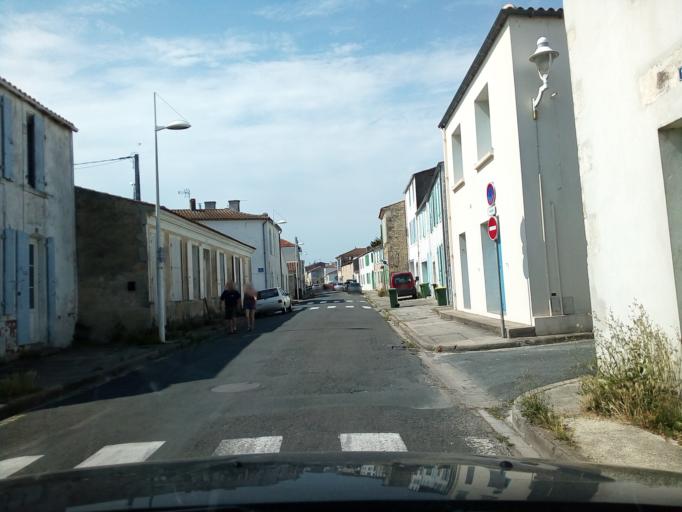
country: FR
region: Poitou-Charentes
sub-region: Departement de la Charente-Maritime
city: Dolus-d'Oleron
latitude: 45.9470
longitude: -1.3038
